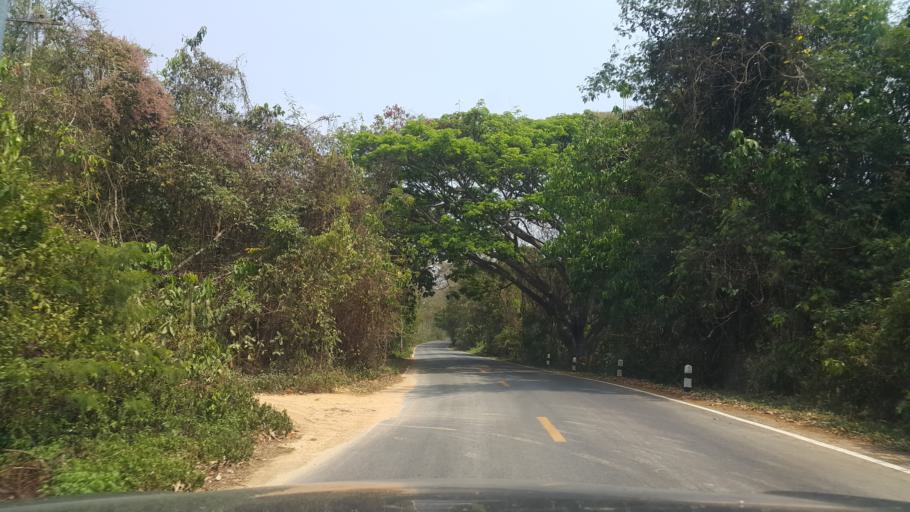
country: TH
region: Lamphun
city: Thung Hua Chang
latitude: 17.9038
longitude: 99.1254
